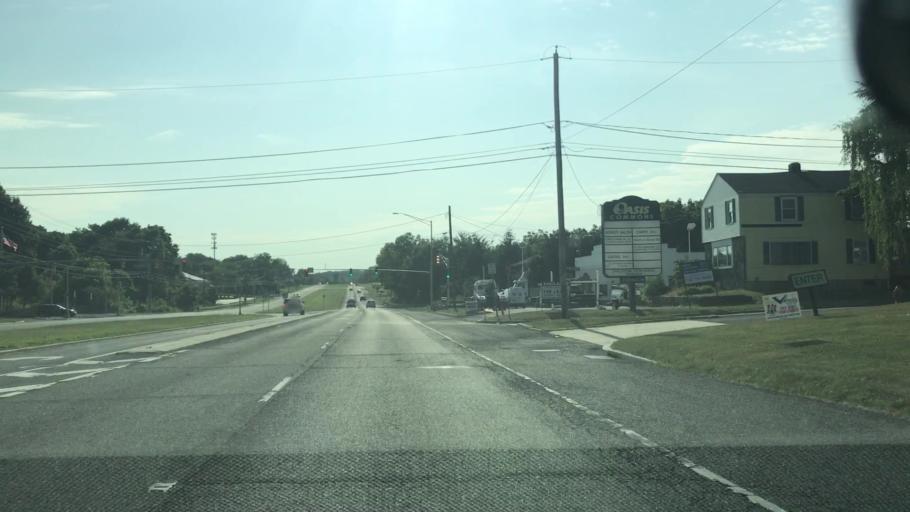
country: US
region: New Jersey
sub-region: Hunterdon County
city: Lebanon
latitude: 40.6438
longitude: -74.8272
